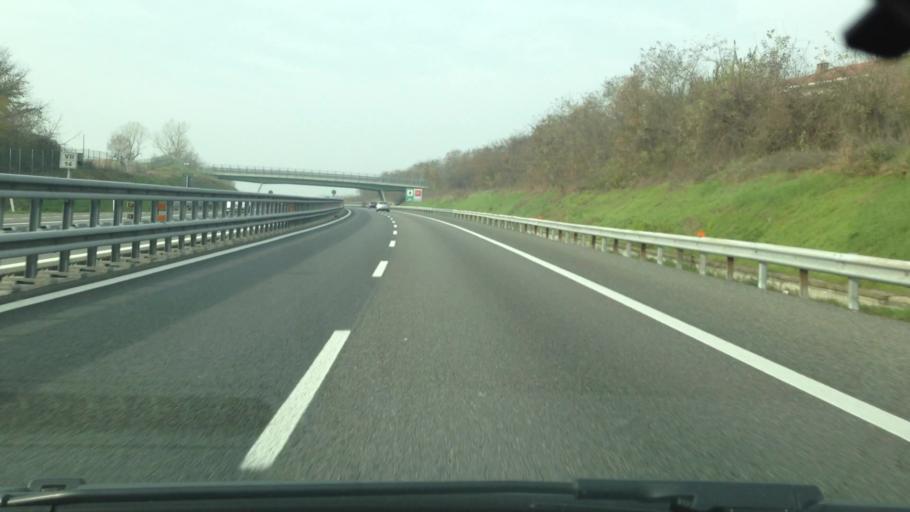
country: IT
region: Piedmont
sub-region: Provincia di Asti
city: San Paolo Solbrito
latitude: 44.9475
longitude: 7.9718
